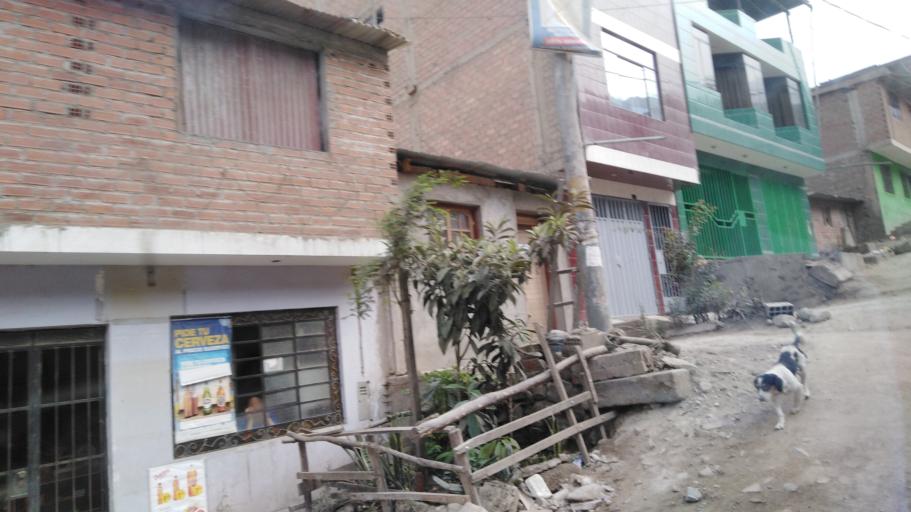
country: PE
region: Lima
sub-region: Lima
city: La Molina
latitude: -12.1469
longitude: -76.9279
